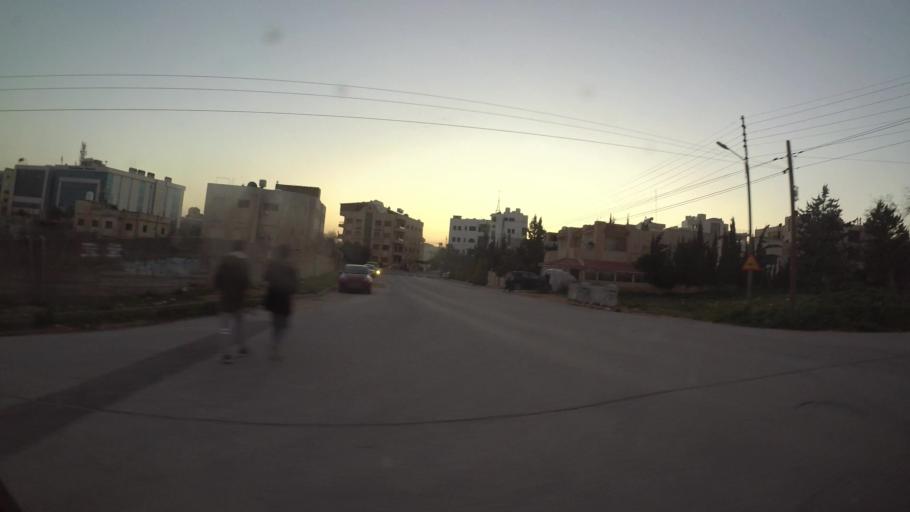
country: JO
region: Amman
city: Al Jubayhah
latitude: 31.9986
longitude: 35.8539
